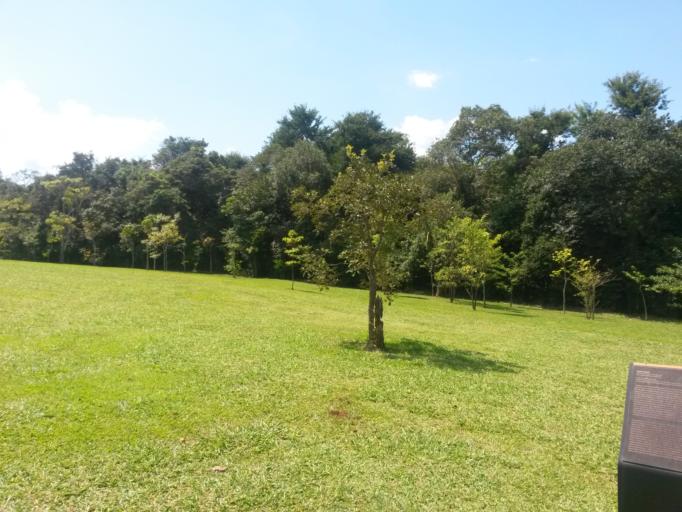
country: BR
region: Minas Gerais
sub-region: Brumadinho
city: Brumadinho
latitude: -20.1252
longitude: -44.2254
